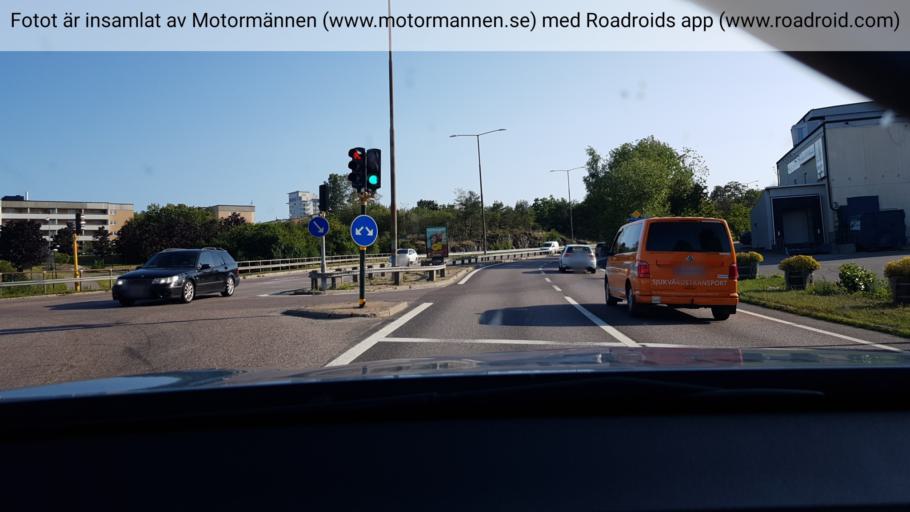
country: SE
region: Stockholm
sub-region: Stockholms Kommun
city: Arsta
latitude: 59.2925
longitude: 18.0295
